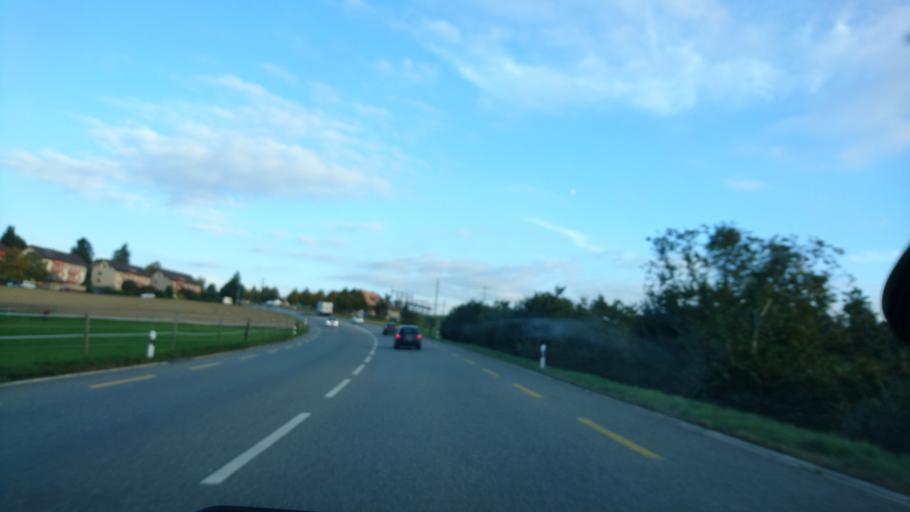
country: CH
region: Bern
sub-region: Bern-Mittelland District
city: Biglen
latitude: 46.9115
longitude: 7.6263
